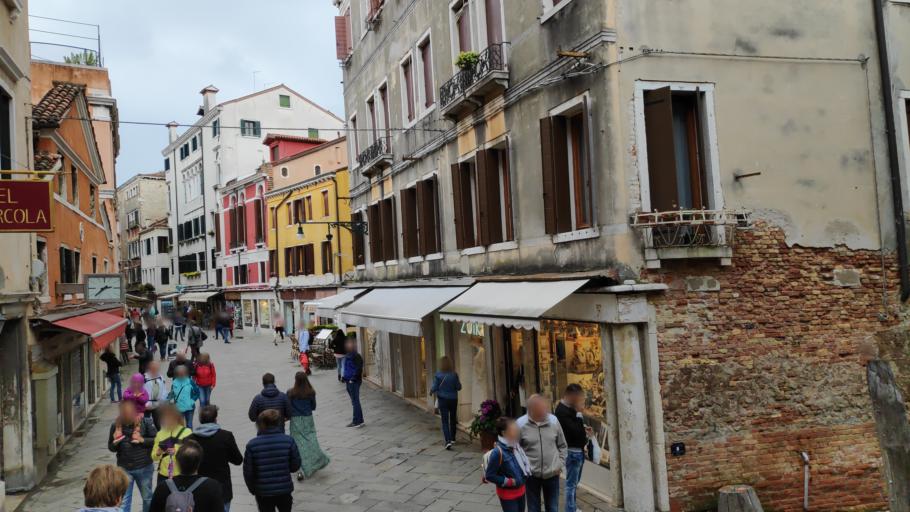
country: IT
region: Veneto
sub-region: Provincia di Venezia
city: Venice
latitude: 45.4437
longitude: 12.3298
